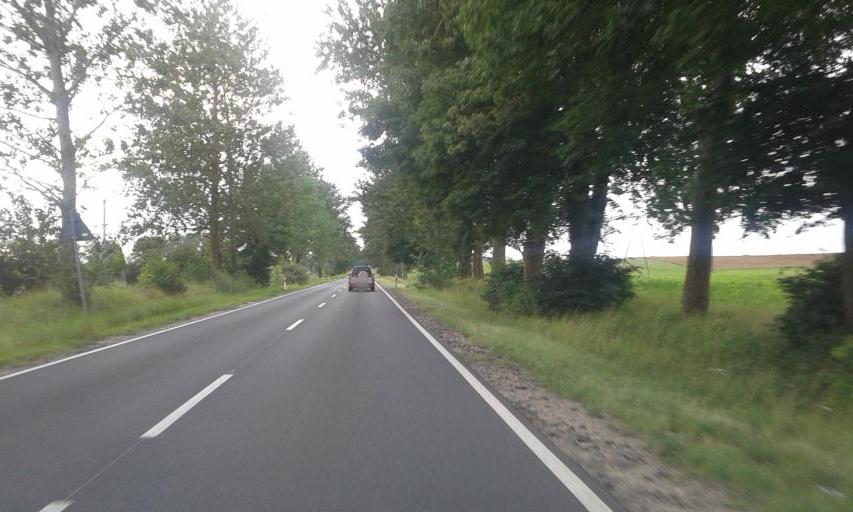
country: PL
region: West Pomeranian Voivodeship
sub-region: Powiat szczecinecki
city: Szczecinek
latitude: 53.7155
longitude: 16.5985
